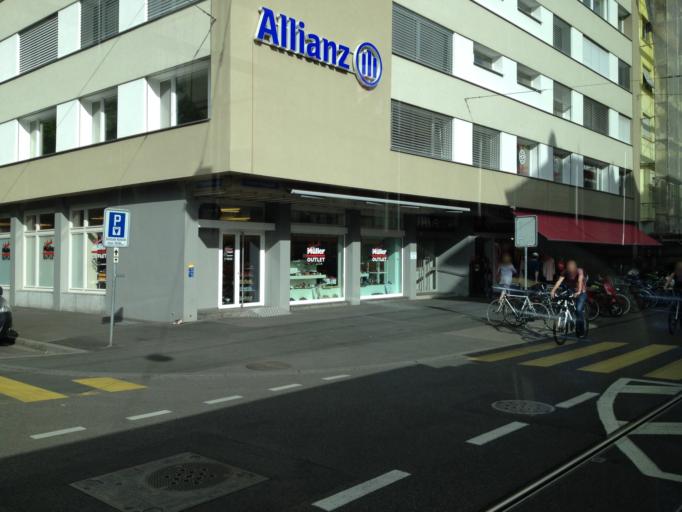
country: CH
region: Basel-City
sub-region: Basel-Stadt
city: Basel
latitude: 47.5631
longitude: 7.5920
